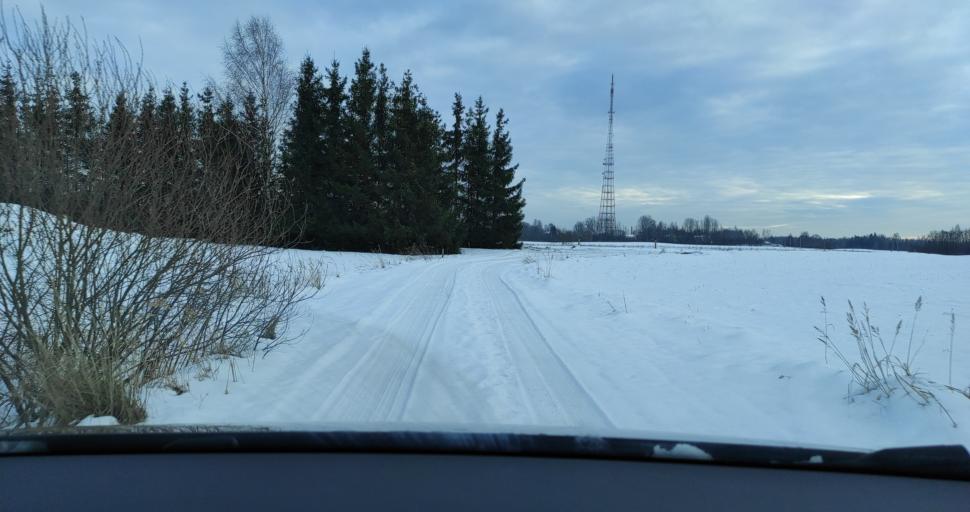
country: LV
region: Kuldigas Rajons
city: Kuldiga
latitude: 56.9418
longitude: 22.0073
